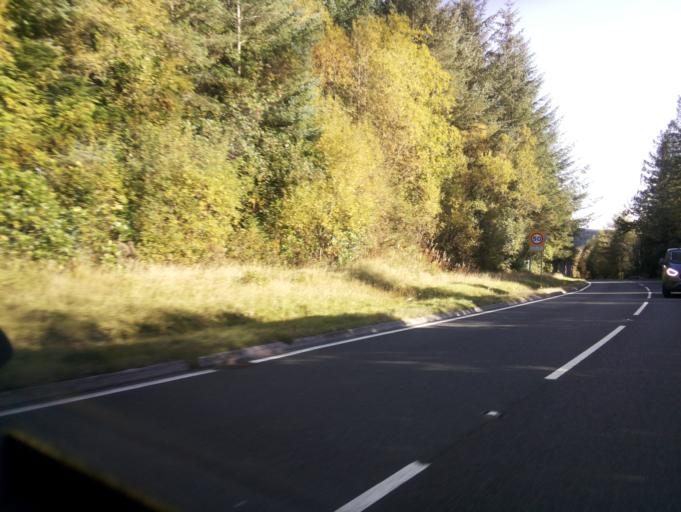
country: GB
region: Wales
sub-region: Rhondda Cynon Taf
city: Hirwaun
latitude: 51.8289
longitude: -3.4569
